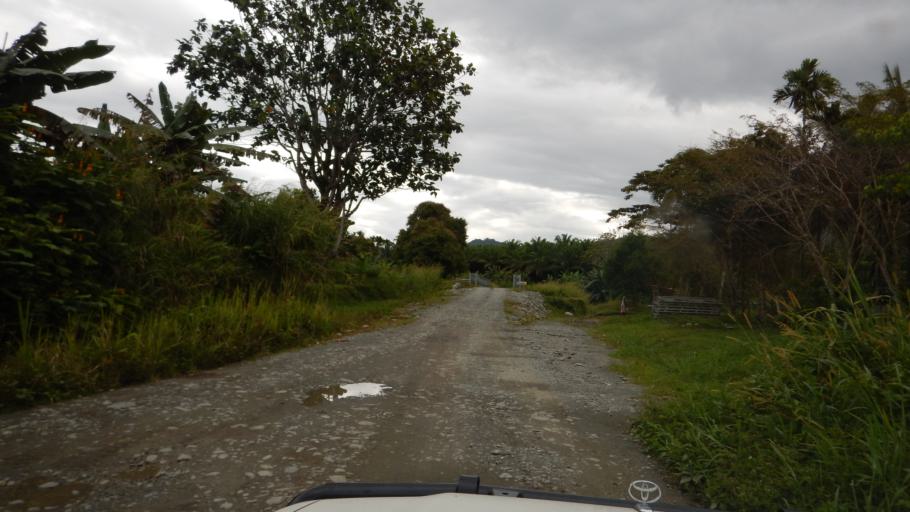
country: PG
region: Northern Province
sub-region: Sohe
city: Kokoda
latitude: -8.9181
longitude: 147.8705
